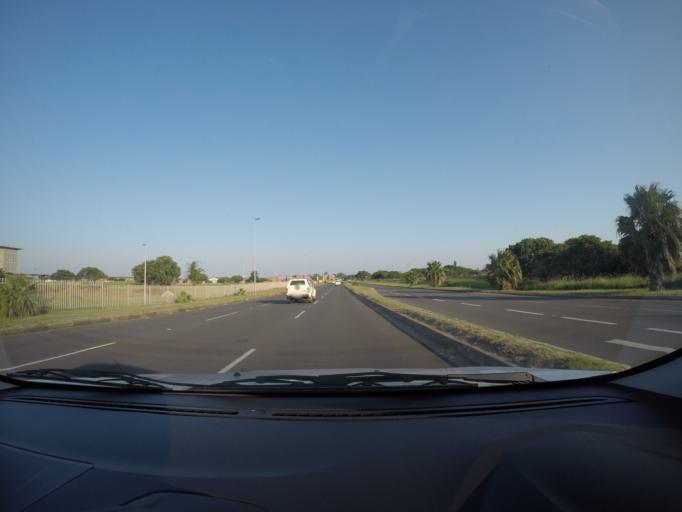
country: ZA
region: KwaZulu-Natal
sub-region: uThungulu District Municipality
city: Richards Bay
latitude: -28.7587
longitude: 32.0487
